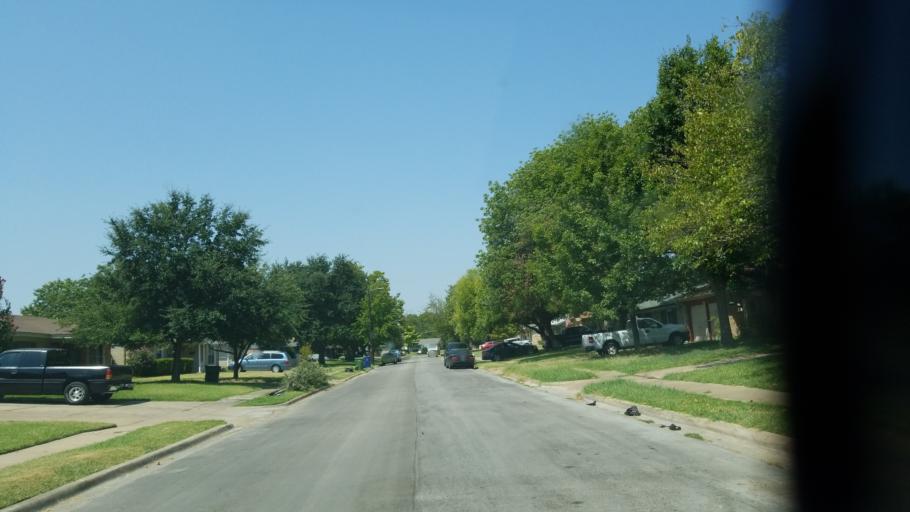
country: US
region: Texas
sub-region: Dallas County
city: Garland
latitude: 32.9269
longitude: -96.6237
